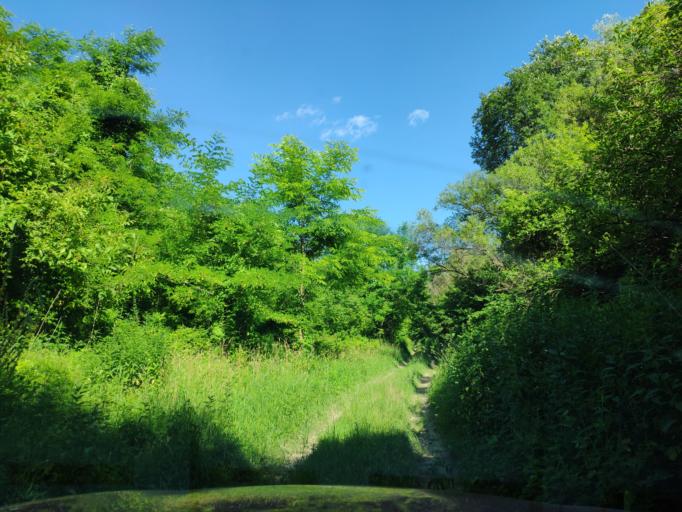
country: SK
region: Banskobystricky
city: Rimavska Sobota
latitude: 48.2565
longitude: 20.1180
